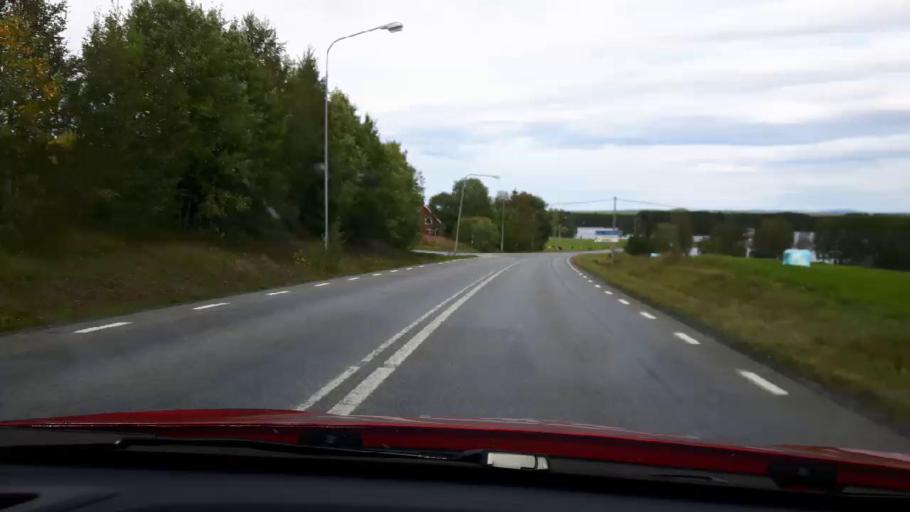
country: SE
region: Jaemtland
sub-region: Krokoms Kommun
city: Valla
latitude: 63.2412
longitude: 14.0010
